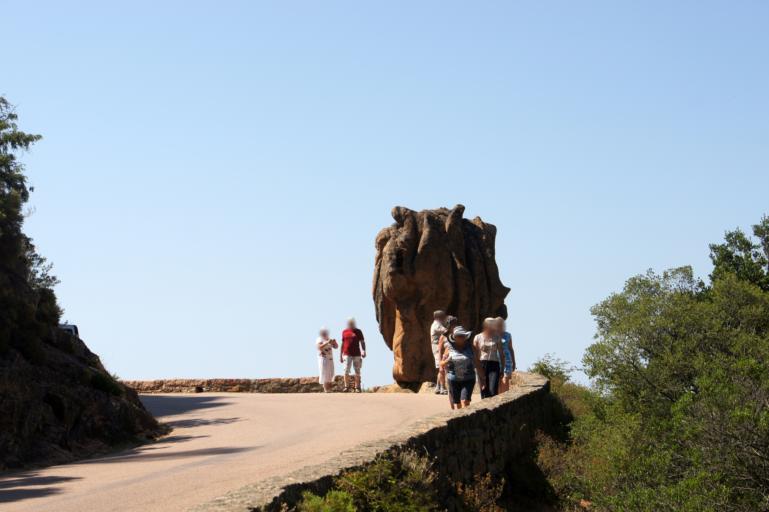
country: FR
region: Corsica
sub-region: Departement de la Corse-du-Sud
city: Cargese
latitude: 42.2479
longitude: 8.6549
